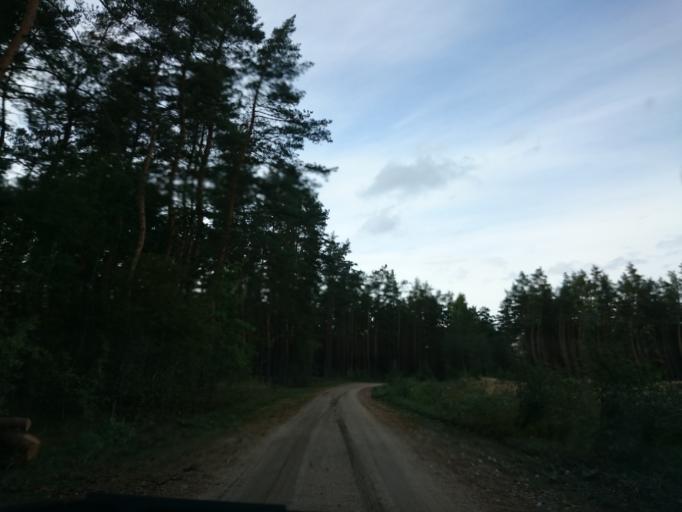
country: LV
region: Garkalne
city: Garkalne
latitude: 57.0403
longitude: 24.3883
